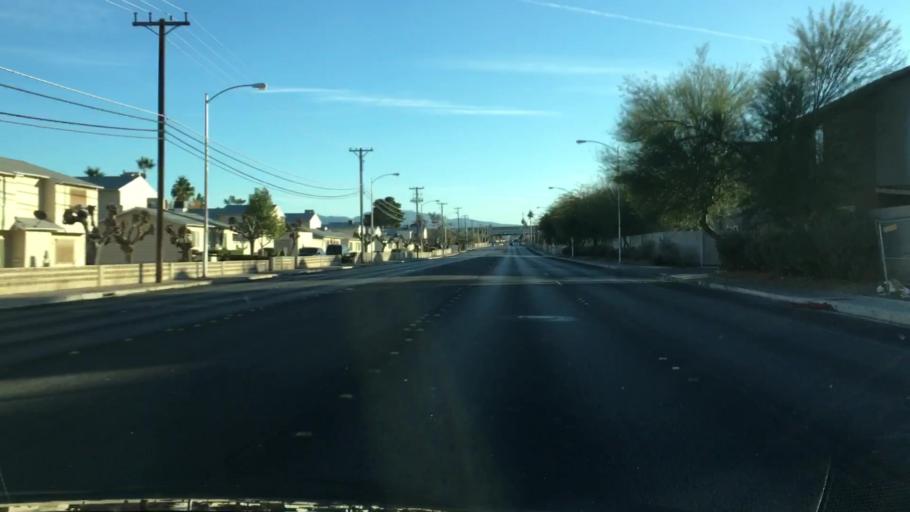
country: US
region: Nevada
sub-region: Clark County
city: Whitney
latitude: 36.0986
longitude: -115.0733
